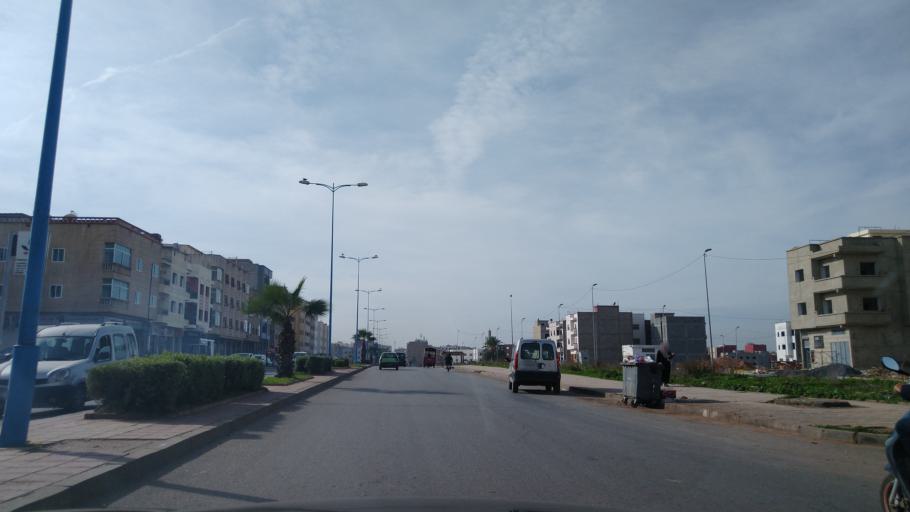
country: MA
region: Grand Casablanca
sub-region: Mohammedia
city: Mohammedia
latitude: 33.6837
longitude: -7.3810
